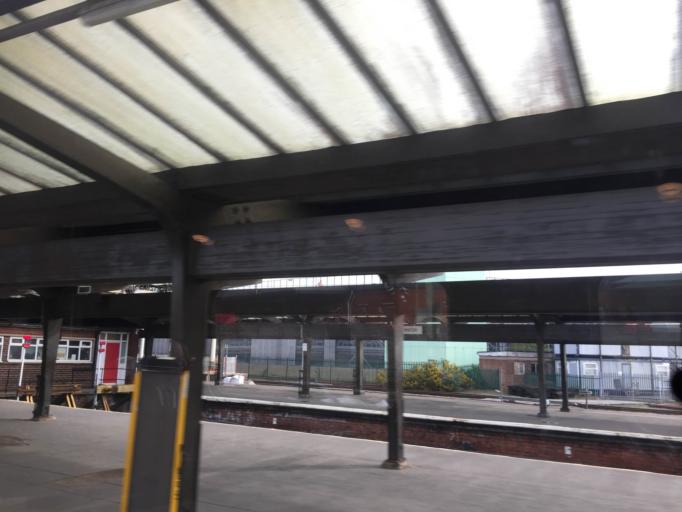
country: GB
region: England
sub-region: Lancashire
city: Preston
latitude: 53.7538
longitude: -2.7069
